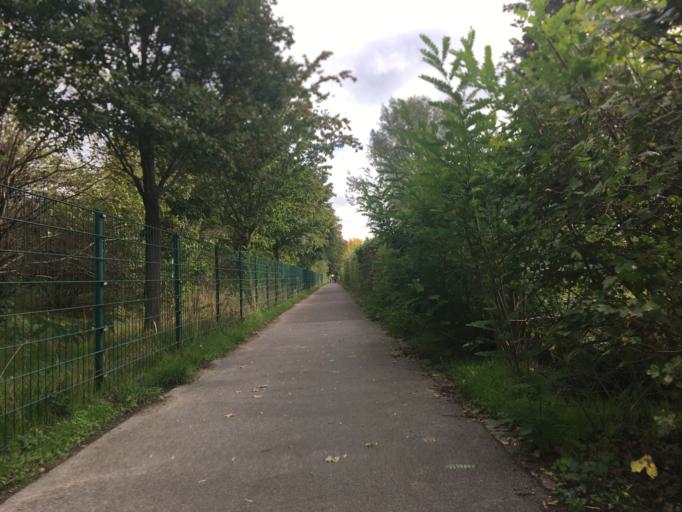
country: DE
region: Berlin
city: Kladow
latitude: 52.4624
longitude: 13.1502
